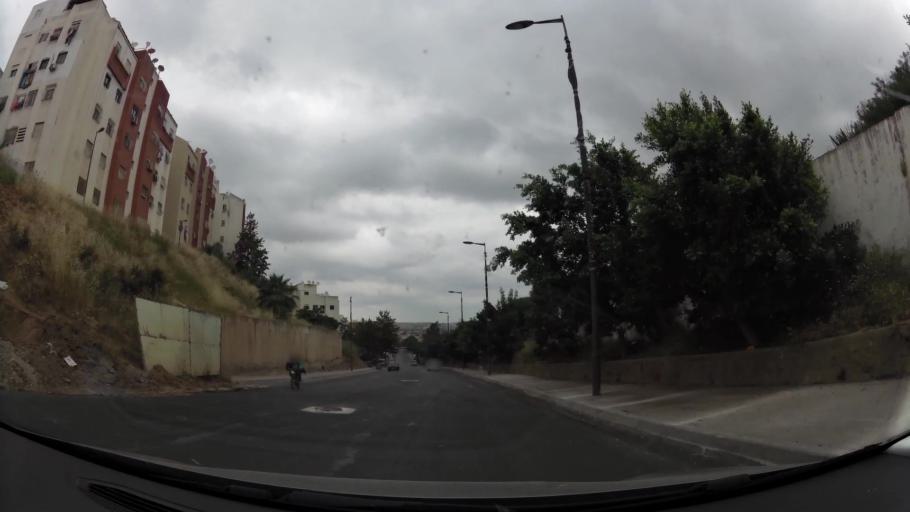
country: MA
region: Rabat-Sale-Zemmour-Zaer
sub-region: Rabat
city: Rabat
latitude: 33.9838
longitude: -6.8057
